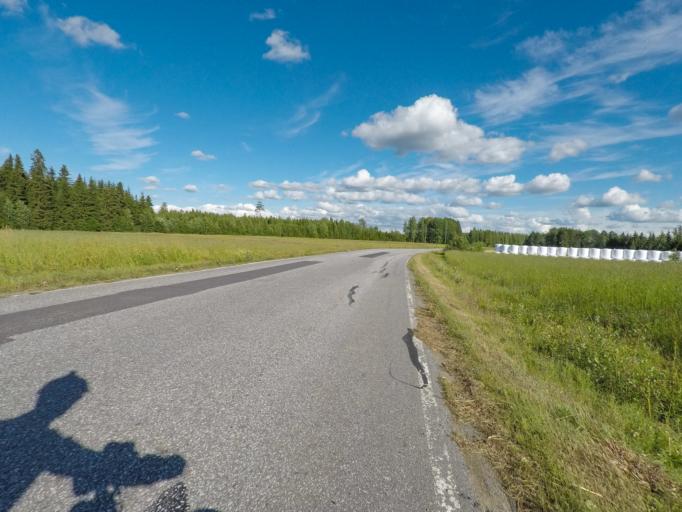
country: FI
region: South Karelia
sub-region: Imatra
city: Imatra
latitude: 61.1364
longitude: 28.6541
